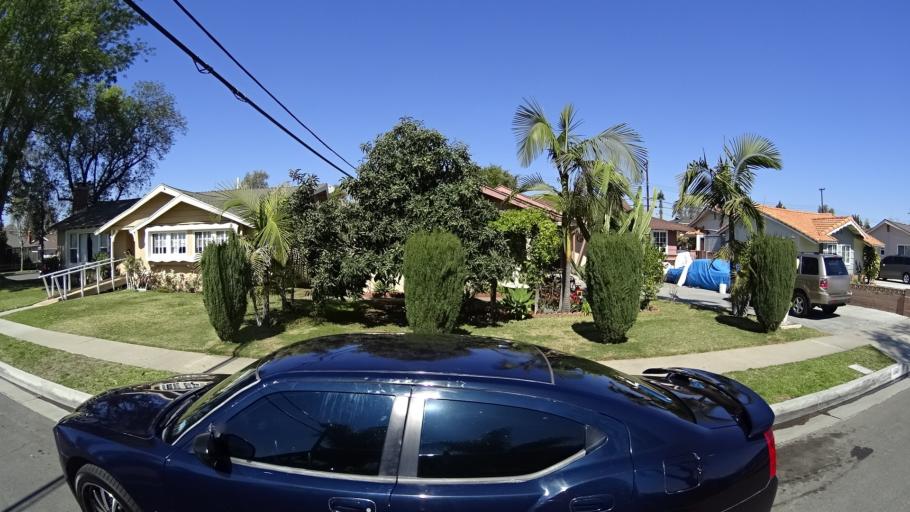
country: US
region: California
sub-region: Orange County
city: Anaheim
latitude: 33.8122
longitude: -117.9362
